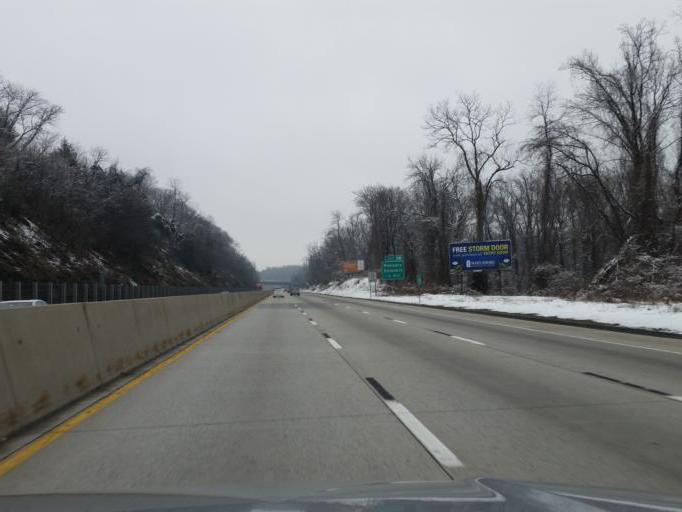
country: US
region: Pennsylvania
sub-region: Cumberland County
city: New Cumberland
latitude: 40.2020
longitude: -76.8689
